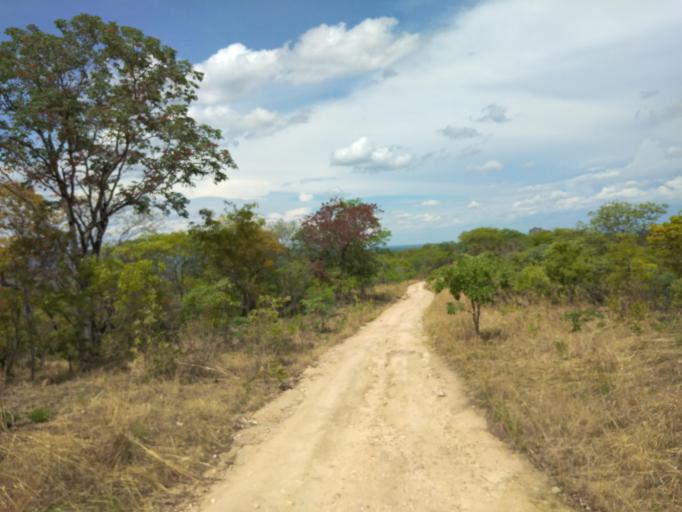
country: ZM
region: Eastern
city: Nyimba
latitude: -14.1178
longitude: 30.1032
